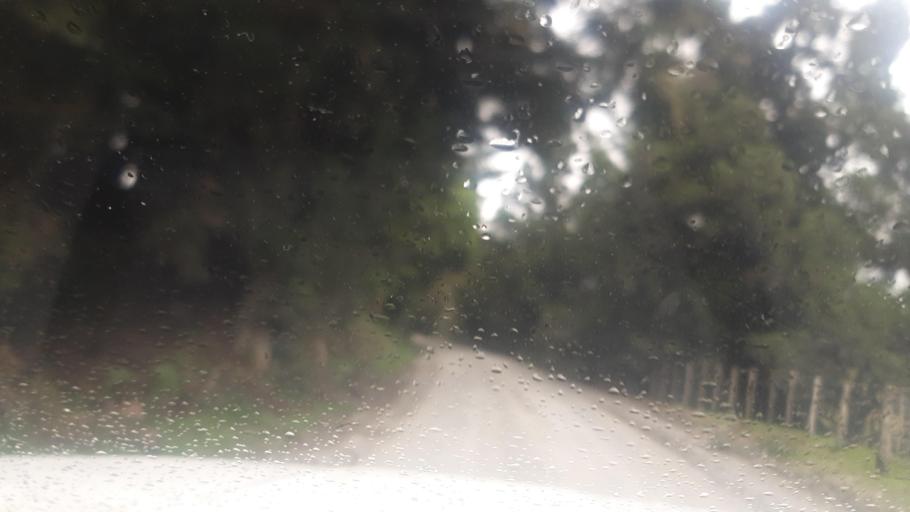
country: NZ
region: Northland
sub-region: Far North District
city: Taipa
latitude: -35.0981
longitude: 173.3972
